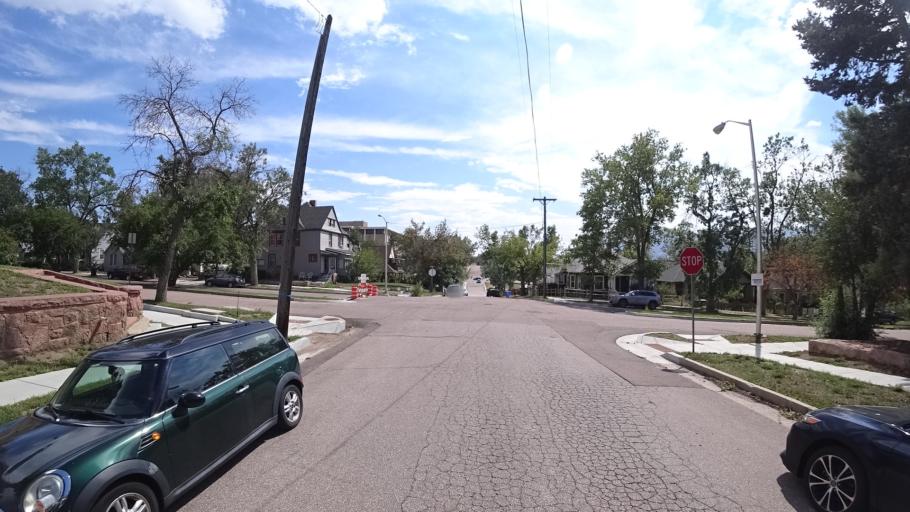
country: US
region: Colorado
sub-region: El Paso County
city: Colorado Springs
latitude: 38.8351
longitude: -104.8105
